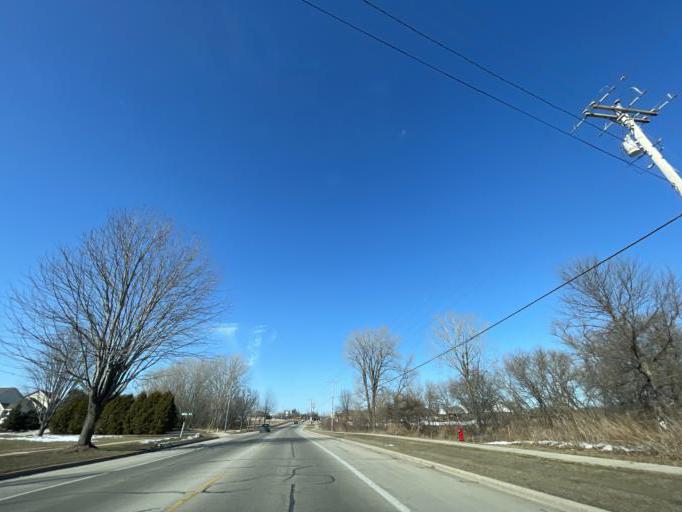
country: US
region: Wisconsin
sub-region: Brown County
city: Howard
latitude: 44.5873
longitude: -88.0843
